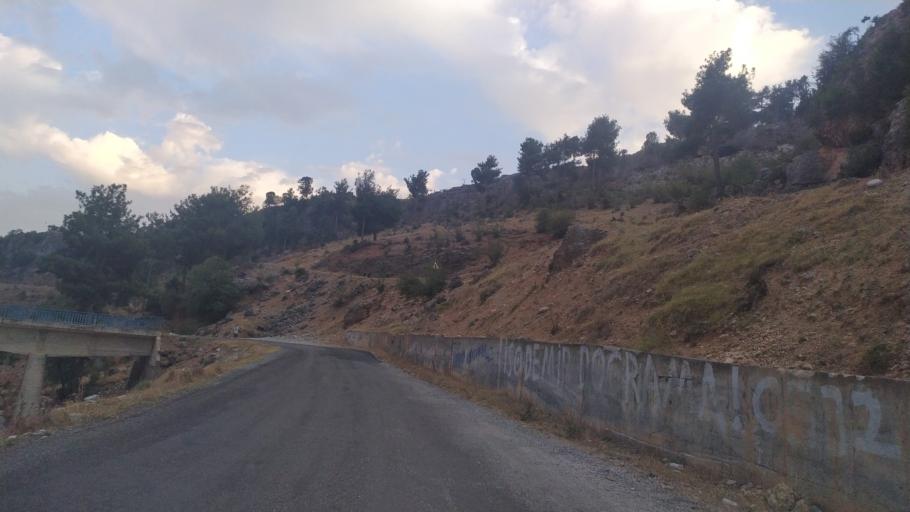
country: TR
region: Mersin
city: Camliyayla
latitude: 37.2403
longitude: 34.7127
